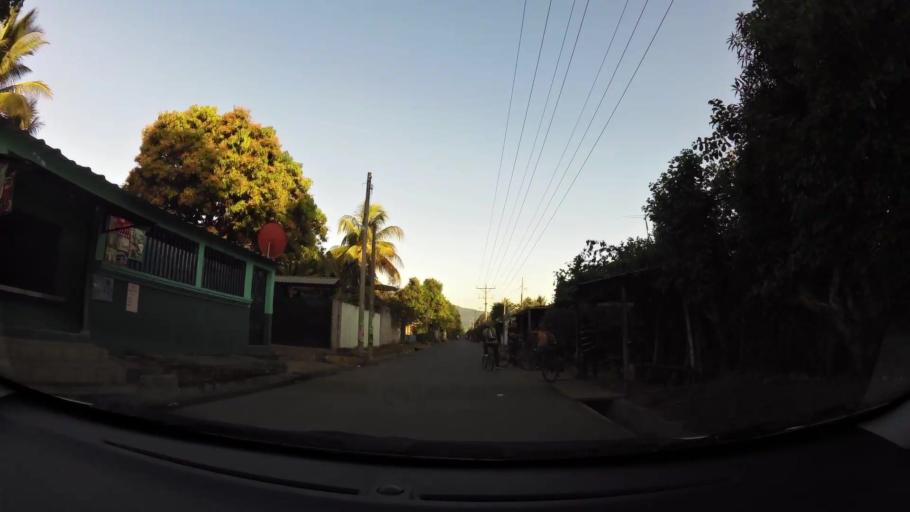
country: SV
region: Sonsonate
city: Armenia
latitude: 13.7418
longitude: -89.3990
